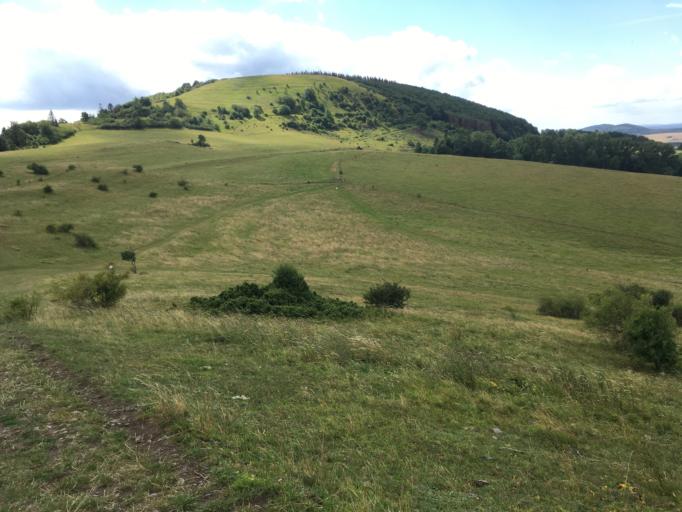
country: DE
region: Hesse
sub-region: Regierungsbezirk Kassel
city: Zierenberg
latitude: 51.3611
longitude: 9.3482
